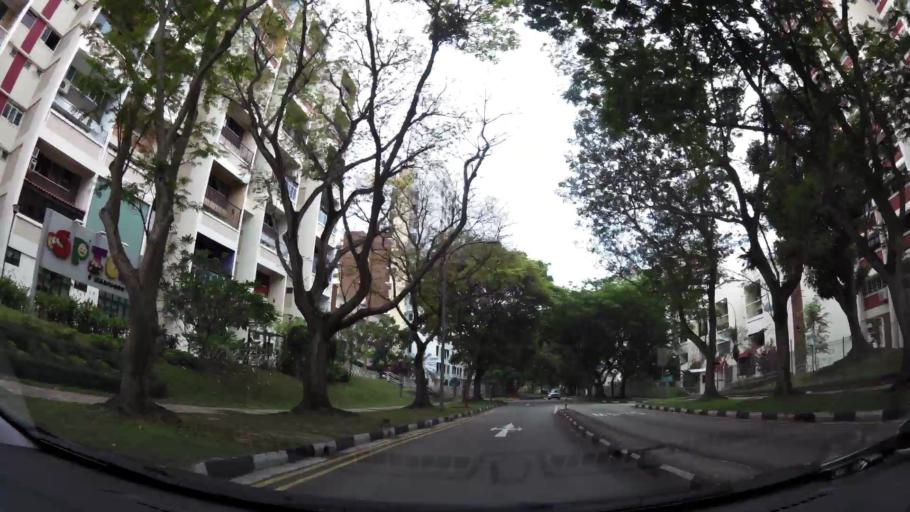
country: SG
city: Singapore
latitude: 1.3664
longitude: 103.8727
